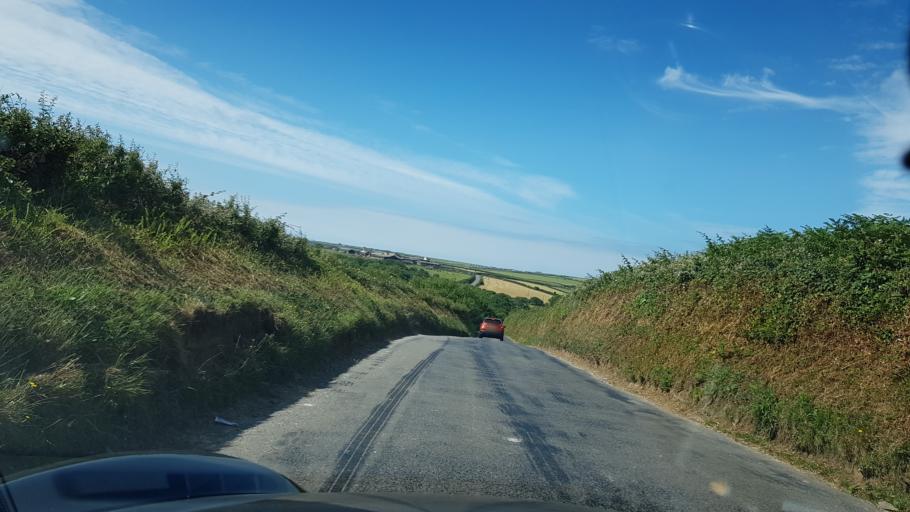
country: GB
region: Wales
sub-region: Pembrokeshire
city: Dale
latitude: 51.7401
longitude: -5.1524
